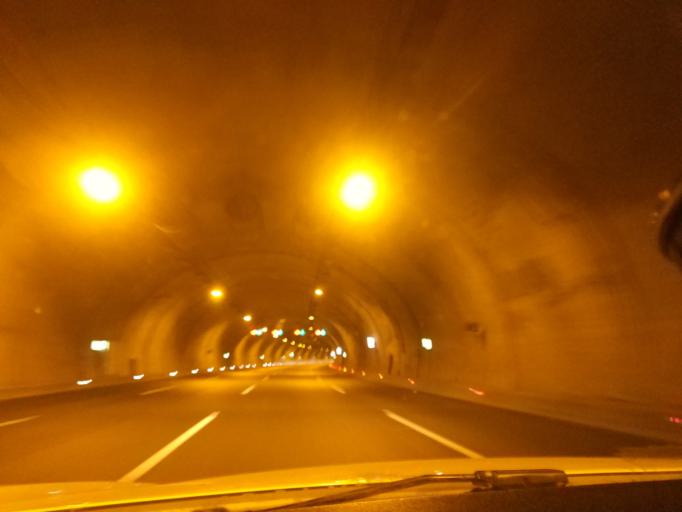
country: TR
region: Istanbul
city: Umraniye
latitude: 41.0545
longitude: 29.1737
